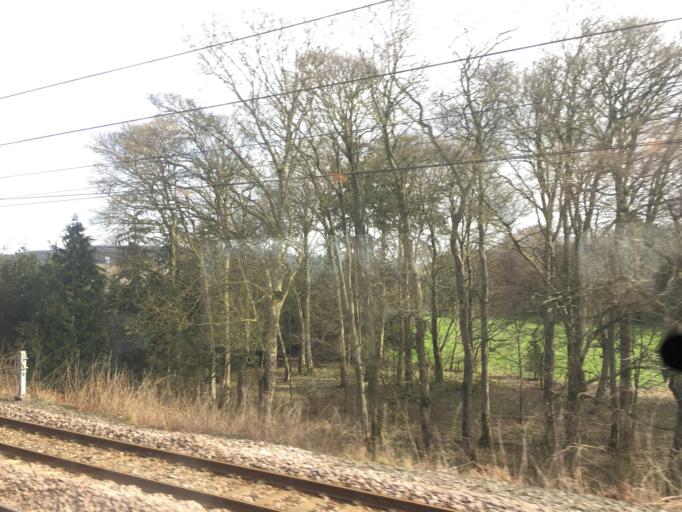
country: GB
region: England
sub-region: Cumbria
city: Penrith
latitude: 54.6508
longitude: -2.7670
